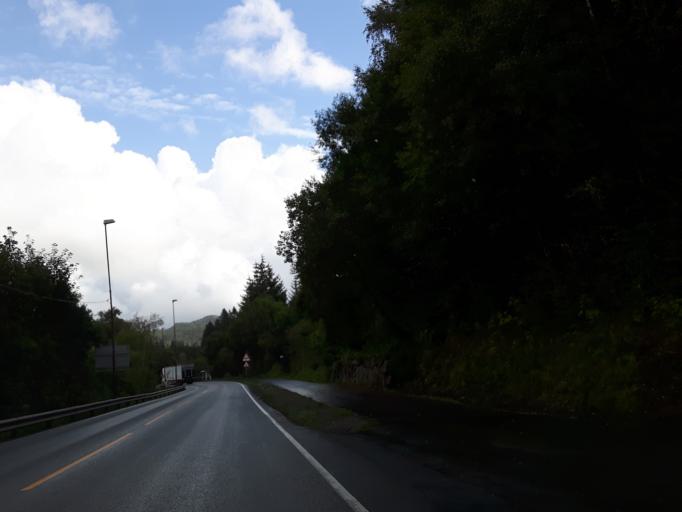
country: NO
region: Vest-Agder
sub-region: Lyngdal
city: Lyngdal
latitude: 58.1487
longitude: 7.0869
